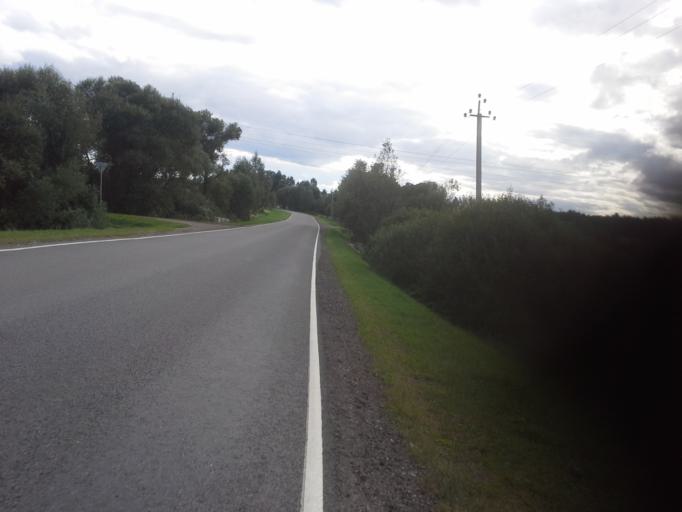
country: RU
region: Moskovskaya
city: Kievskij
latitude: 55.4818
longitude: 36.9070
